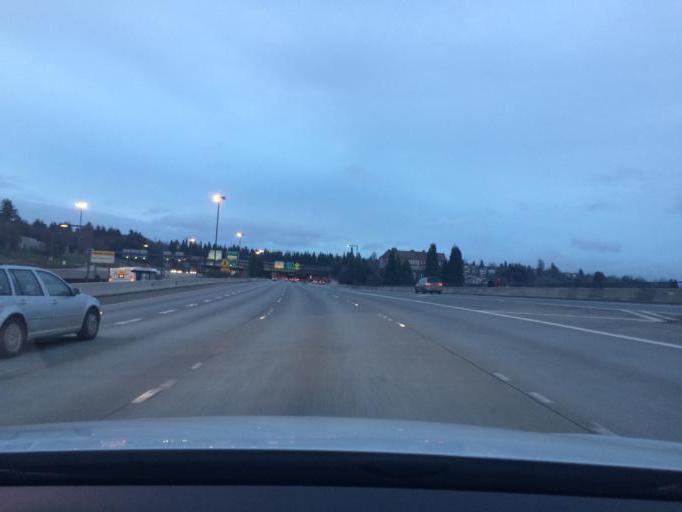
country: US
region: Washington
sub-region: King County
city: Seattle
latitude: 47.5900
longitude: -122.3078
